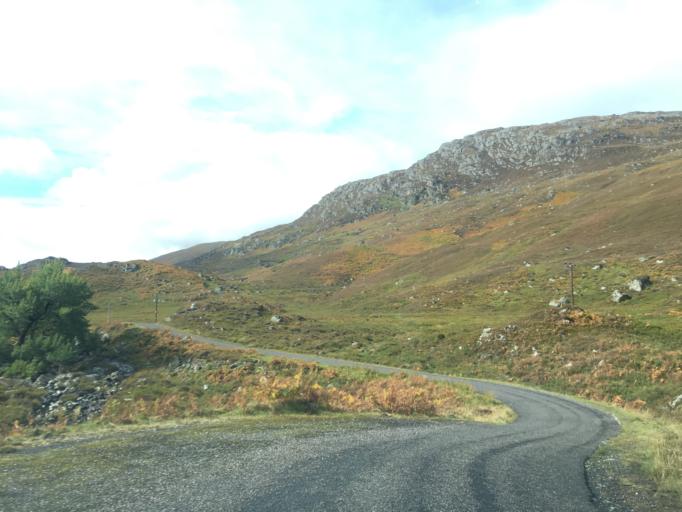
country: GB
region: Scotland
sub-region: Highland
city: Spean Bridge
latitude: 57.3410
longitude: -4.9503
